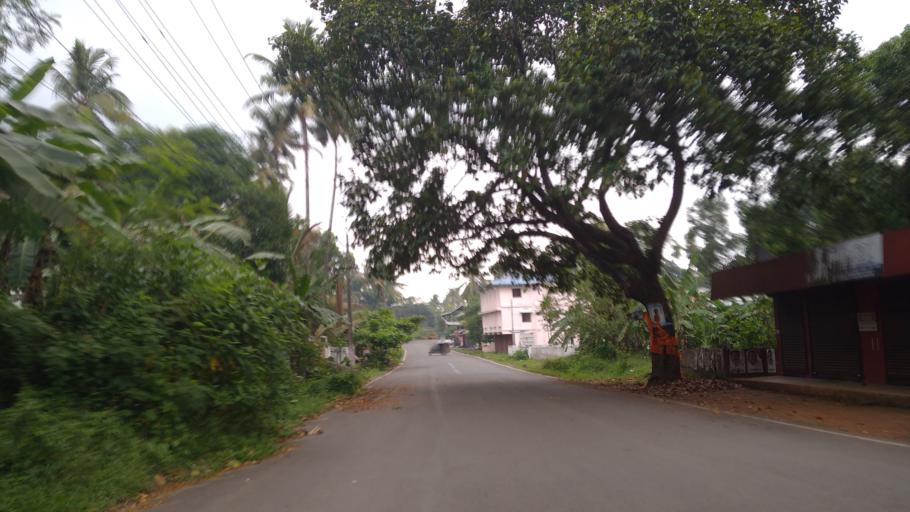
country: IN
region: Kerala
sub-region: Ernakulam
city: Perumbavoor
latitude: 10.0576
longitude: 76.5065
